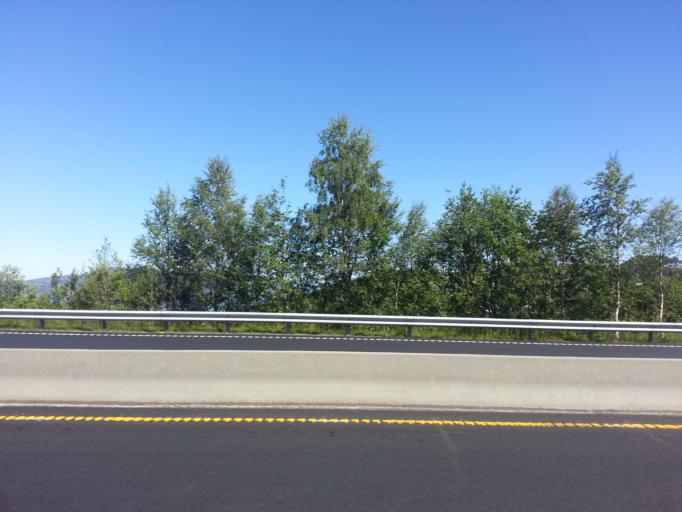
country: NO
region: Sor-Trondelag
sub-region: Malvik
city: Malvik
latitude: 63.4225
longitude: 10.7319
